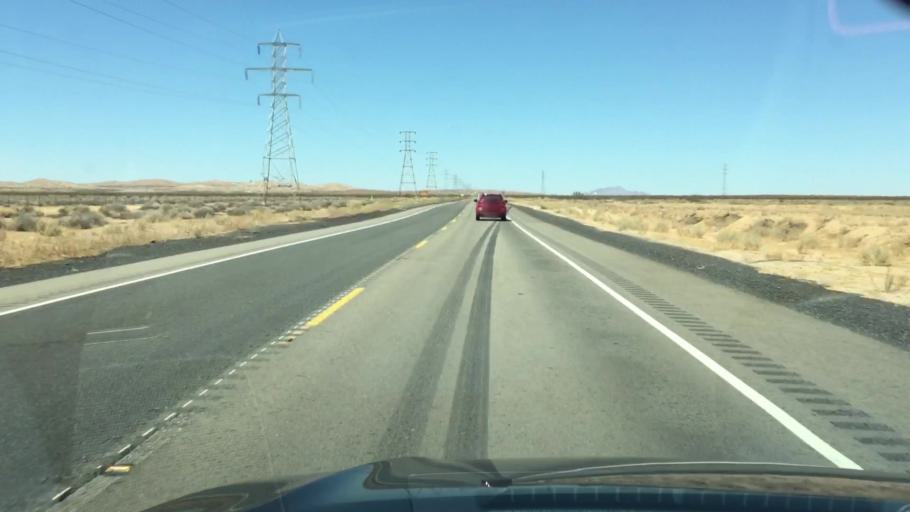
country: US
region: California
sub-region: Kern County
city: Boron
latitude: 35.0319
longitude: -117.5526
